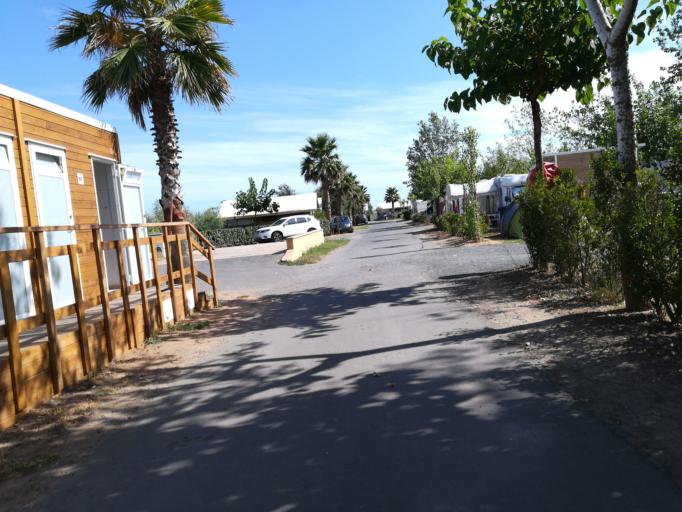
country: FR
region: Languedoc-Roussillon
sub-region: Departement de l'Herault
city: Portiragnes
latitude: 43.2841
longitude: 3.3675
